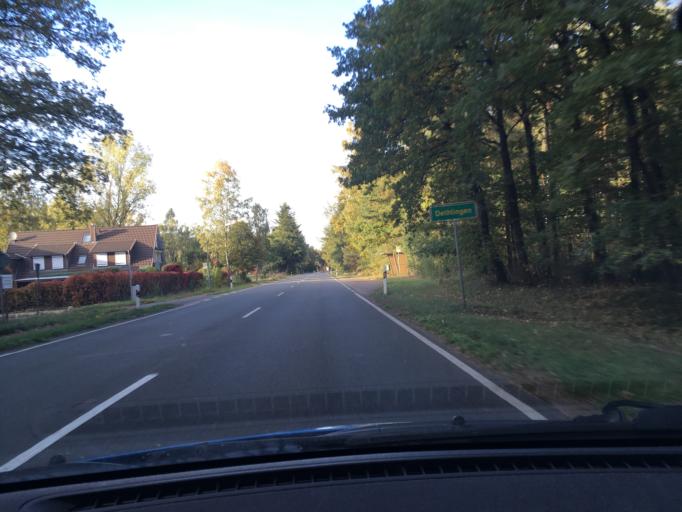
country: DE
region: Lower Saxony
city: Munster
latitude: 52.9503
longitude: 10.1291
